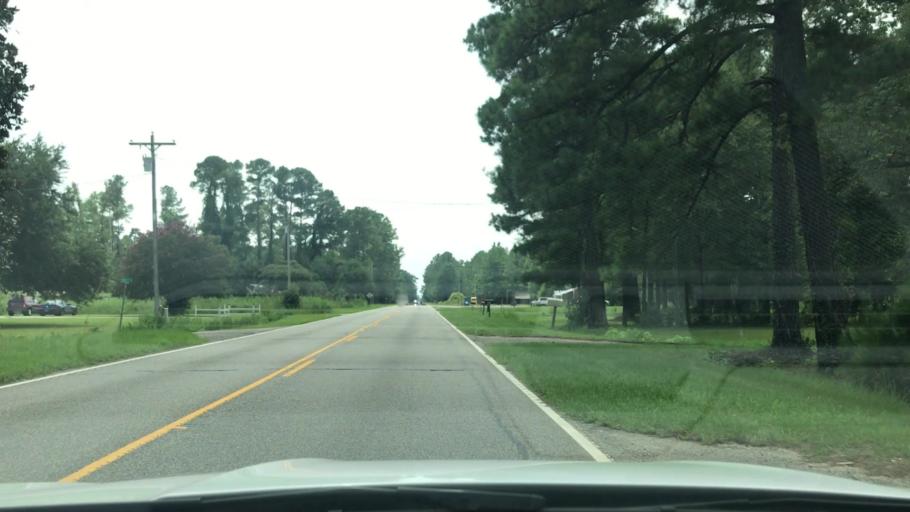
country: US
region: South Carolina
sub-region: Georgetown County
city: Murrells Inlet
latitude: 33.5542
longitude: -79.2176
